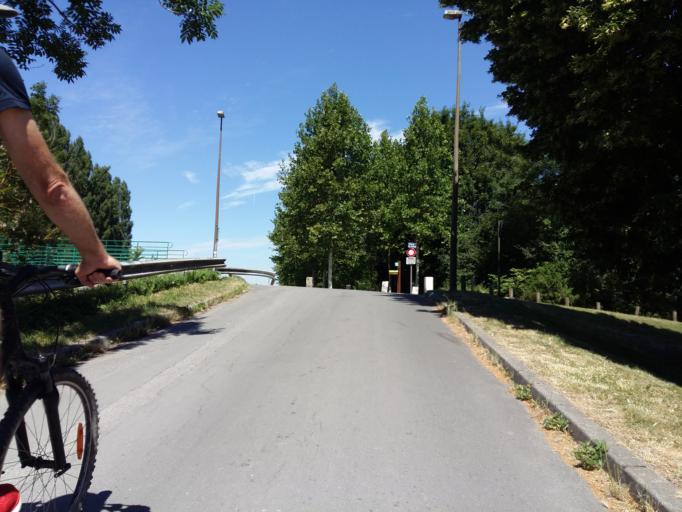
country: FR
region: Picardie
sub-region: Departement de la Somme
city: Amiens
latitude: 49.9092
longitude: 2.2814
